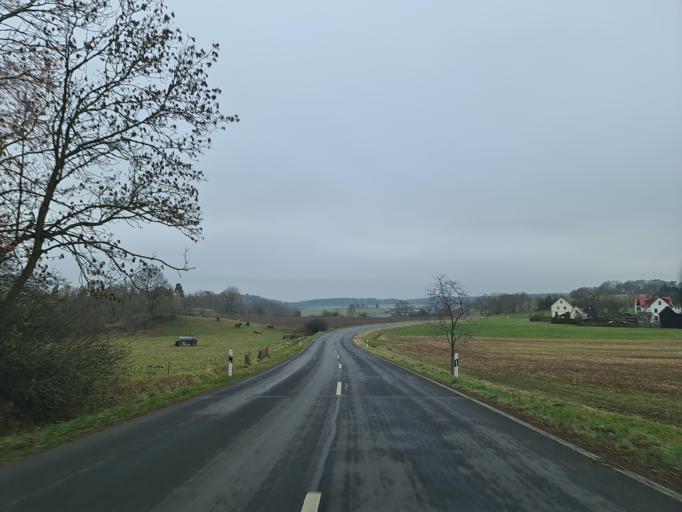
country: DE
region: Saxony
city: Syrau
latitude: 50.5062
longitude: 12.0631
